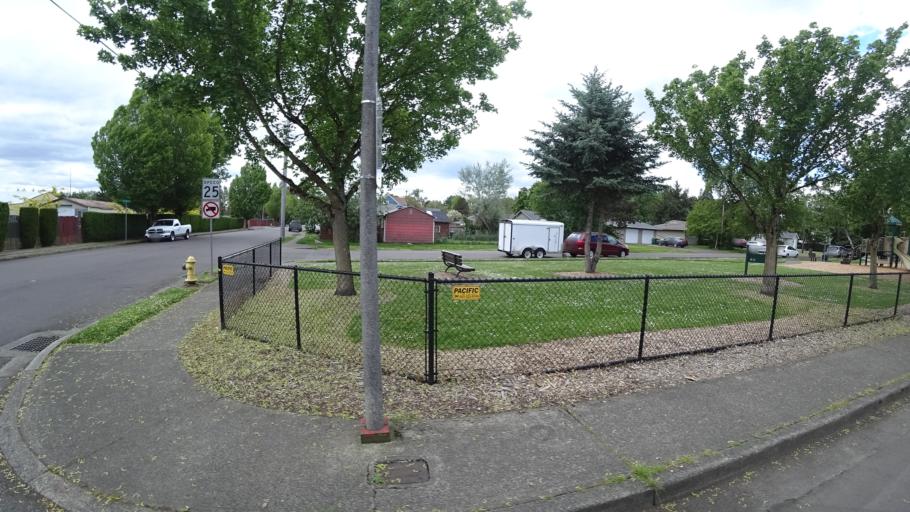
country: US
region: Oregon
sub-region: Washington County
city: Beaverton
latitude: 45.4826
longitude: -122.7968
